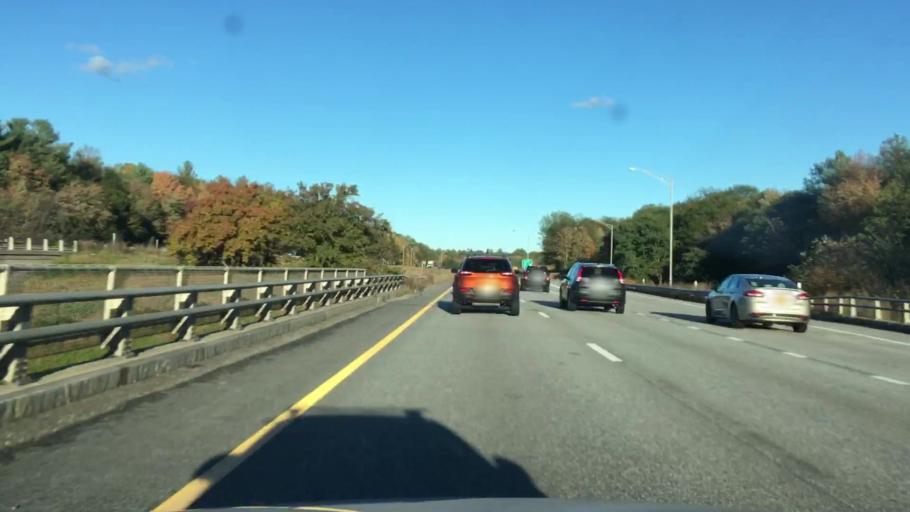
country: US
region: New Hampshire
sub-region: Rockingham County
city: Raymond
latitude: 43.0297
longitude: -71.1649
